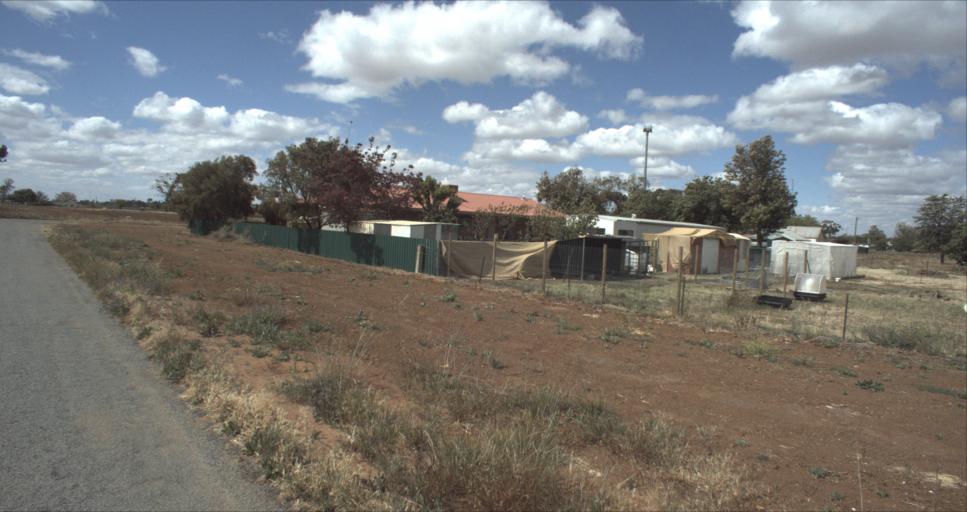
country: AU
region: New South Wales
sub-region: Leeton
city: Leeton
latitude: -34.5923
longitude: 146.4091
